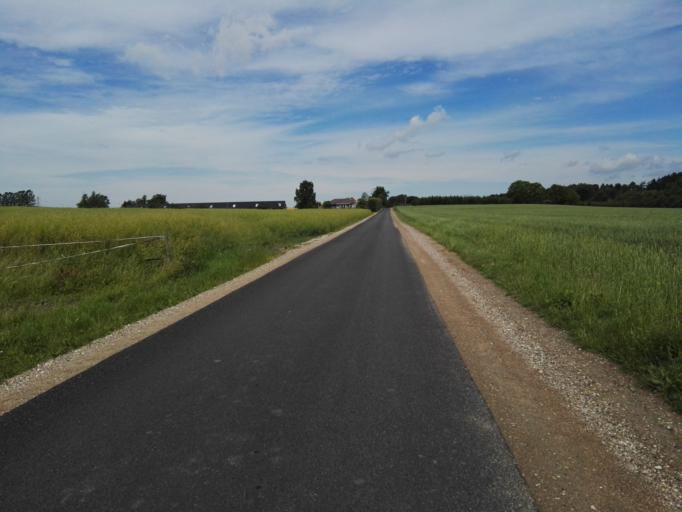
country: DK
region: Capital Region
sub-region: Egedal Kommune
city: Olstykke
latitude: 55.8119
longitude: 12.1782
